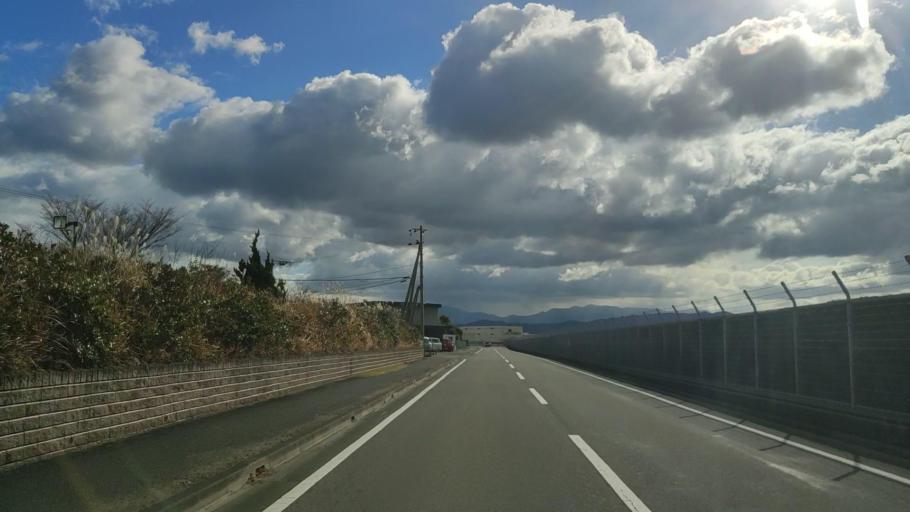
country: JP
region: Ehime
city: Masaki-cho
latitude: 33.8235
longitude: 132.7090
